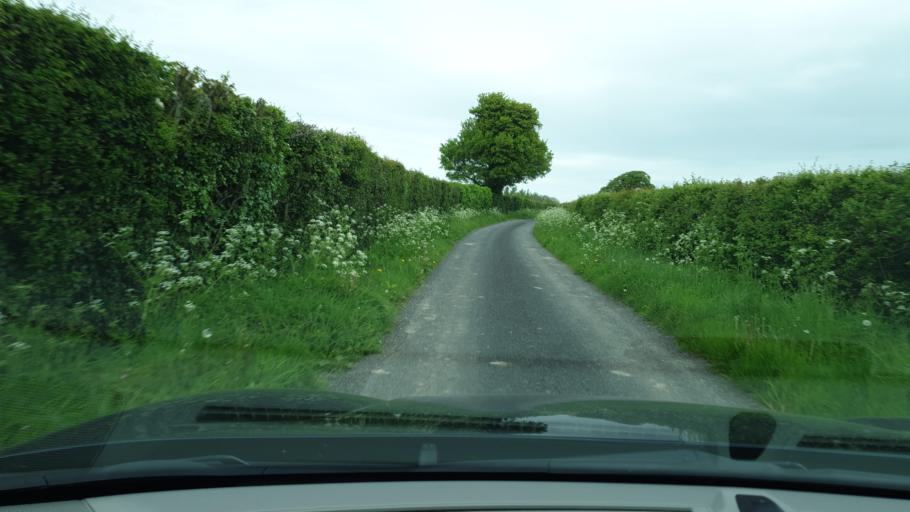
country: IE
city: Confey
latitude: 53.4270
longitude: -6.5336
